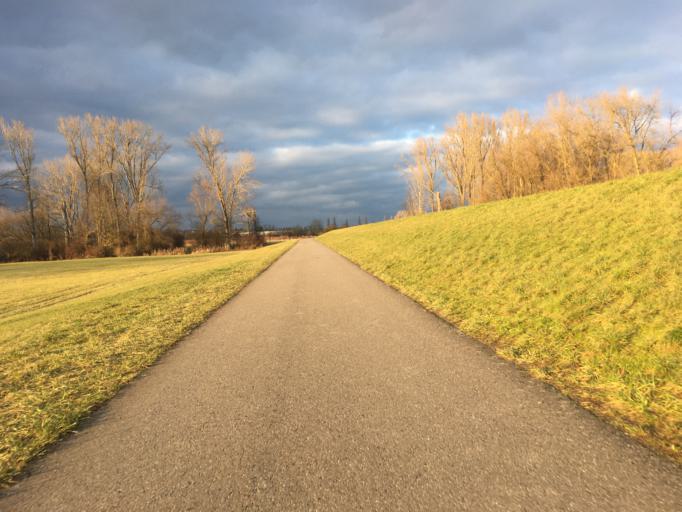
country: DE
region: Rheinland-Pfalz
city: Speyer
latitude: 49.2834
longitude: 8.4199
